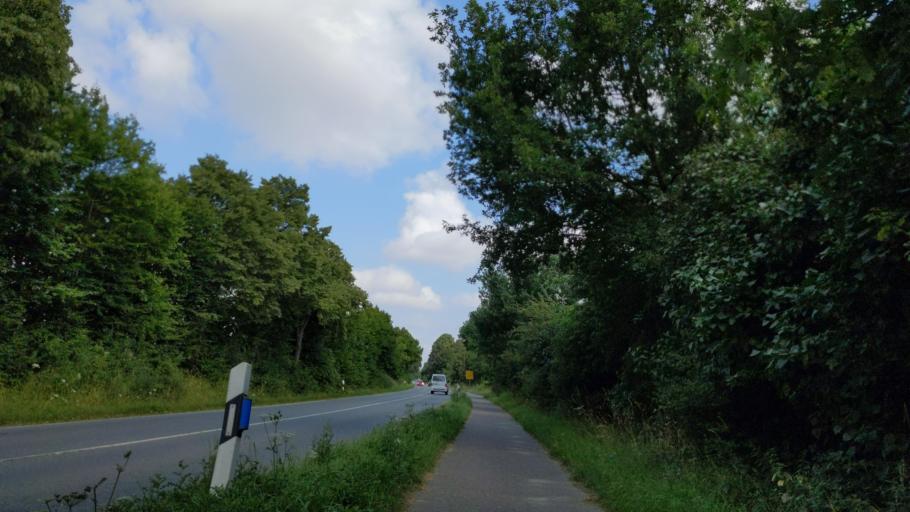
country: DE
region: Schleswig-Holstein
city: Stockelsdorf
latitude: 53.9228
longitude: 10.6390
